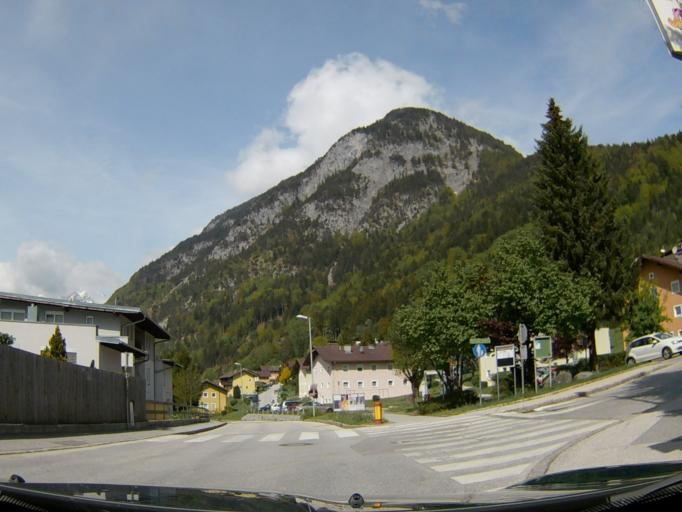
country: AT
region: Tyrol
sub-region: Politischer Bezirk Schwaz
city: Jenbach
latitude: 47.3919
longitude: 11.7674
